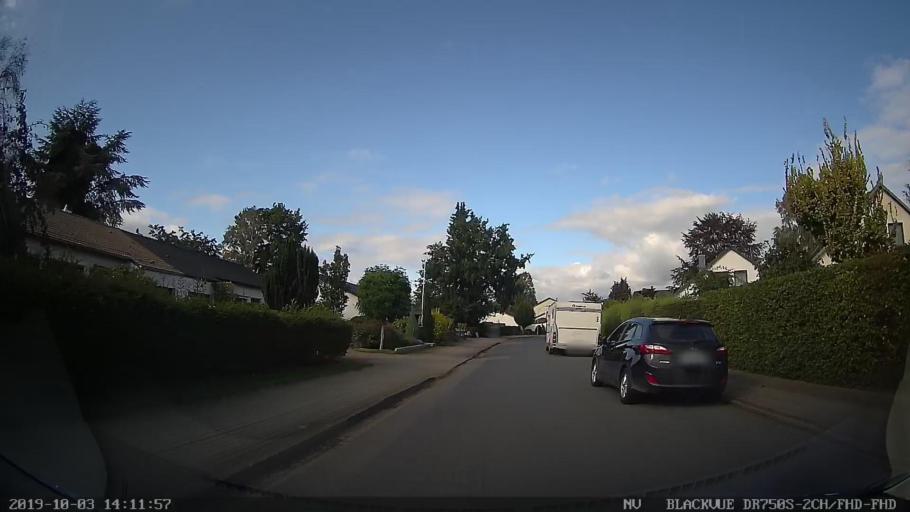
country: DE
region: Schleswig-Holstein
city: Rellingen
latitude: 53.6596
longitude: 9.8313
